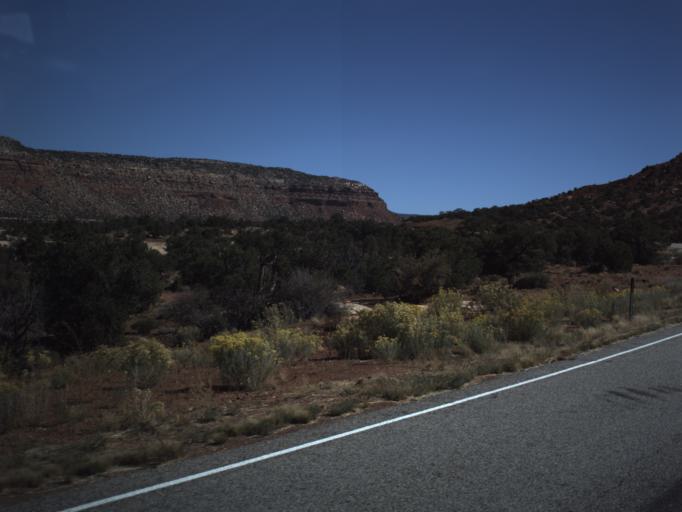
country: US
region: Utah
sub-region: San Juan County
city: Blanding
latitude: 37.6031
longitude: -110.0761
